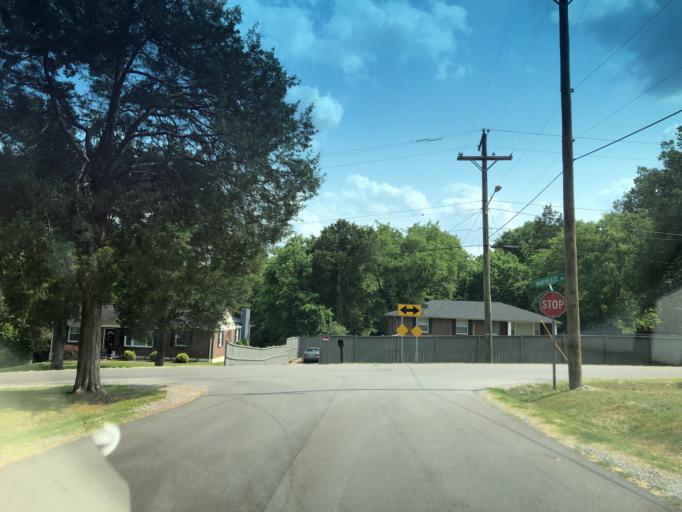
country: US
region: Tennessee
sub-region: Davidson County
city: Goodlettsville
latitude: 36.2580
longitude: -86.7312
